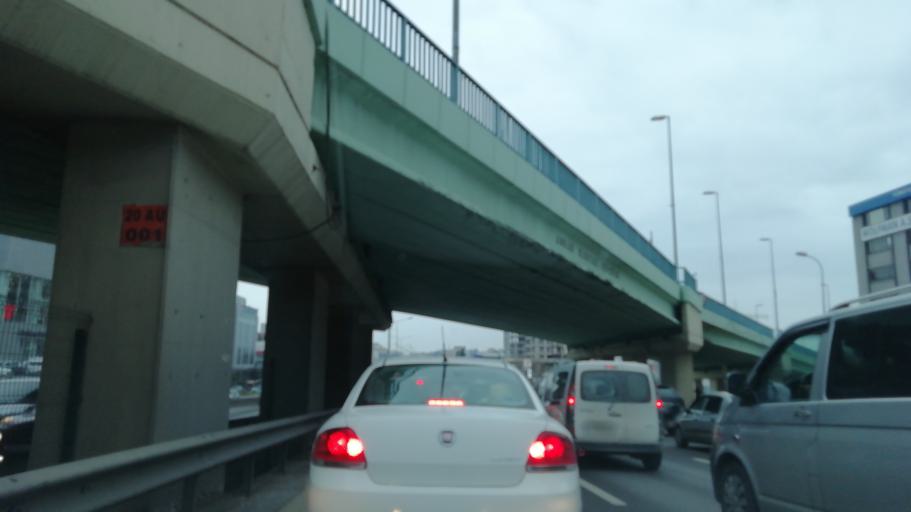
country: TR
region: Istanbul
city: Pendik
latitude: 40.8954
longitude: 29.2277
